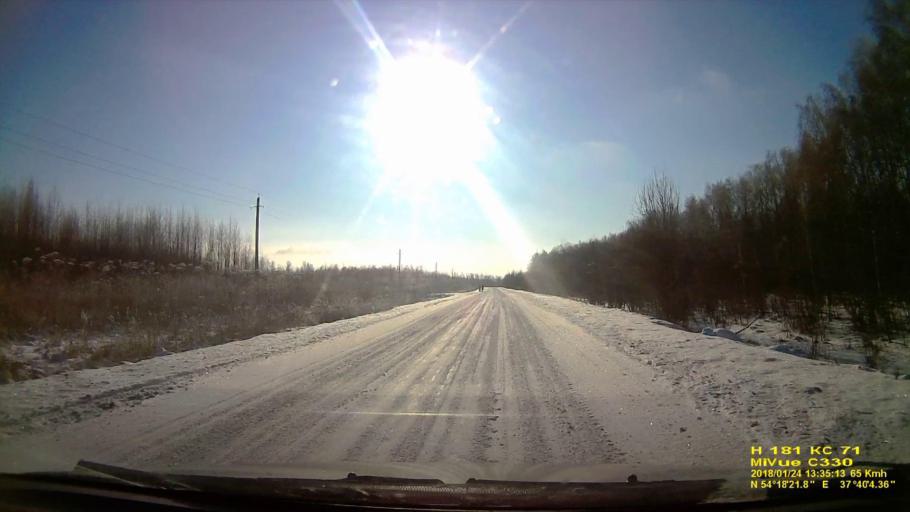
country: RU
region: Tula
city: Revyakino
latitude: 54.3058
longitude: 37.6677
